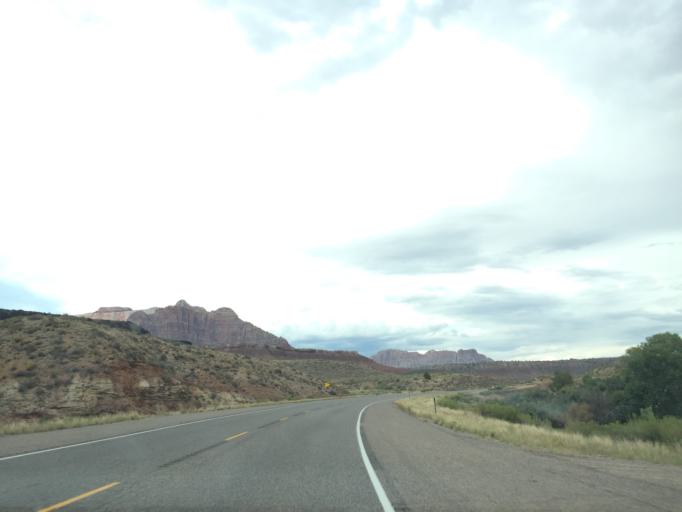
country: US
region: Utah
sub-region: Washington County
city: LaVerkin
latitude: 37.1716
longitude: -113.0917
